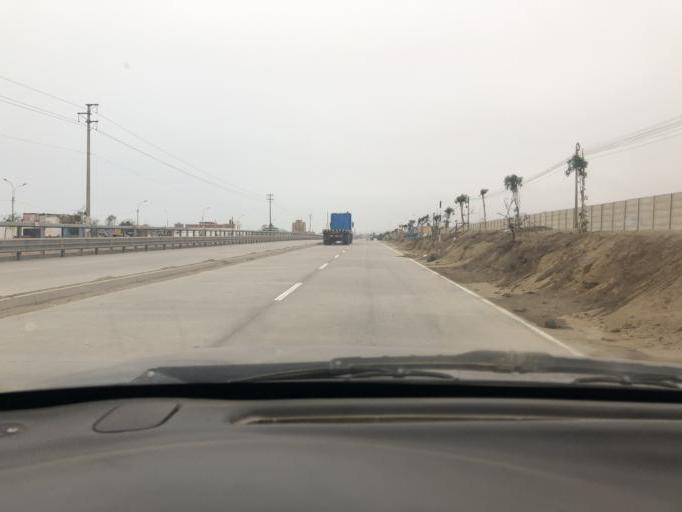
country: PE
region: Lima
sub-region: Lima
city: San Bartolo
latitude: -12.3738
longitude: -76.7855
